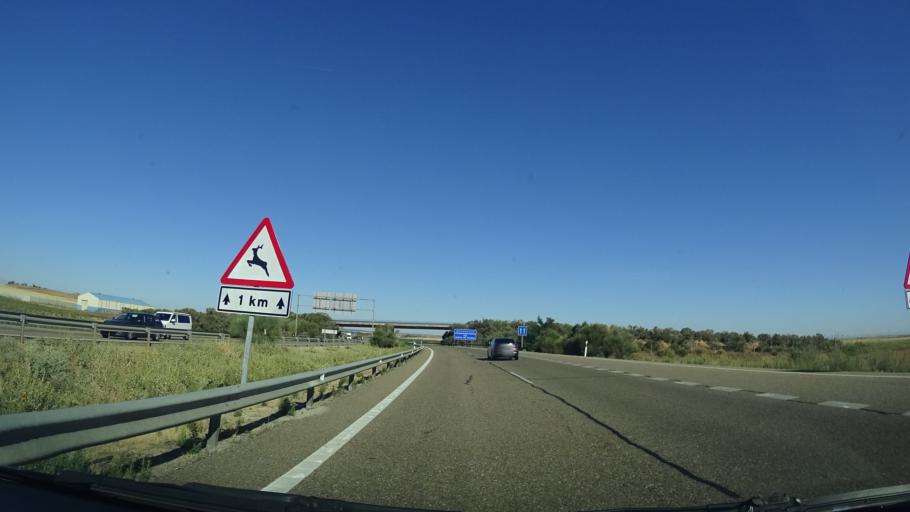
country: ES
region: Castille and Leon
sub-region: Provincia de Valladolid
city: Villardefrades
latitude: 41.7293
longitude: -5.2523
